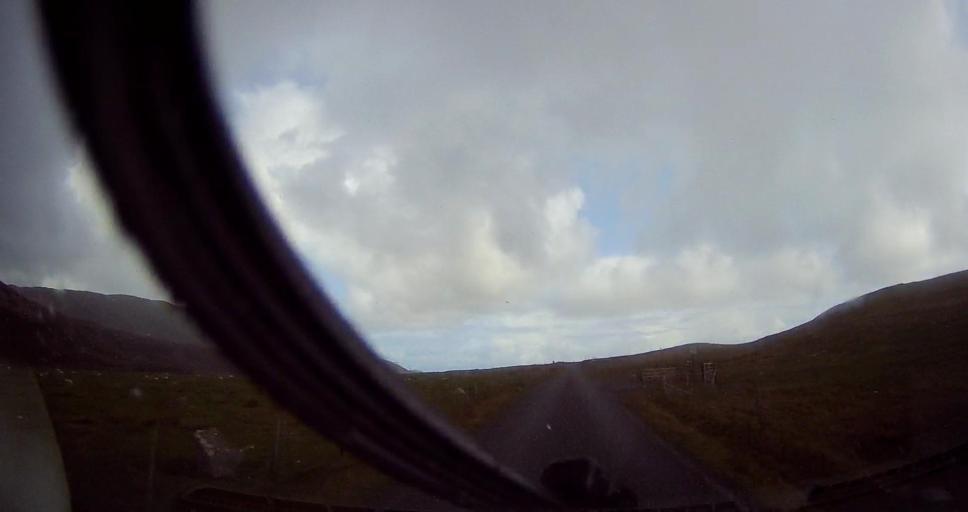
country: GB
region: Scotland
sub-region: Shetland Islands
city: Lerwick
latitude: 60.5542
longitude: -1.3401
